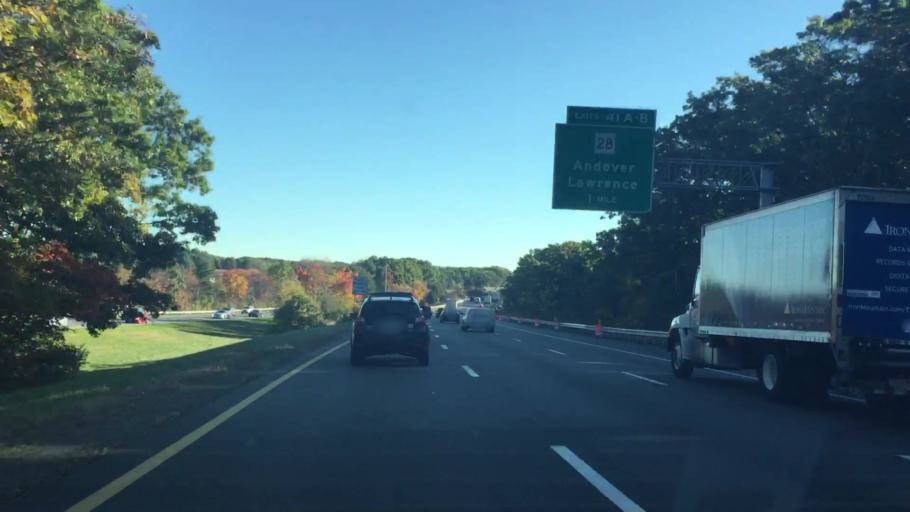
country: US
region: Massachusetts
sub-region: Essex County
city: Lawrence
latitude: 42.6726
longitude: -71.1782
